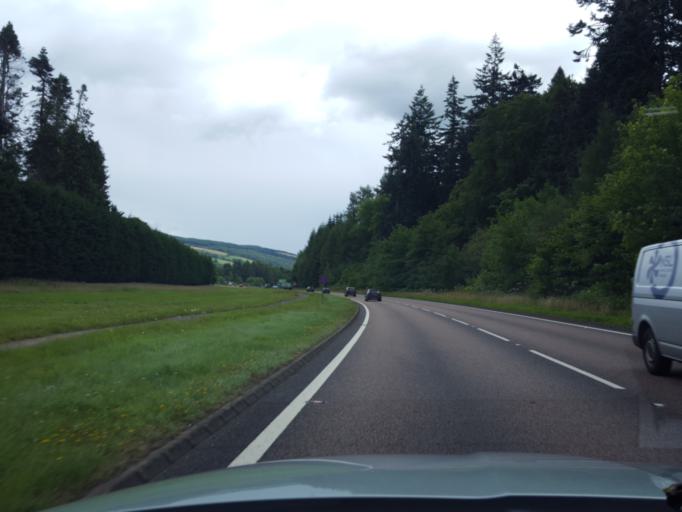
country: GB
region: Scotland
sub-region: Perth and Kinross
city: Pitlochry
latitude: 56.6976
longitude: -3.7446
